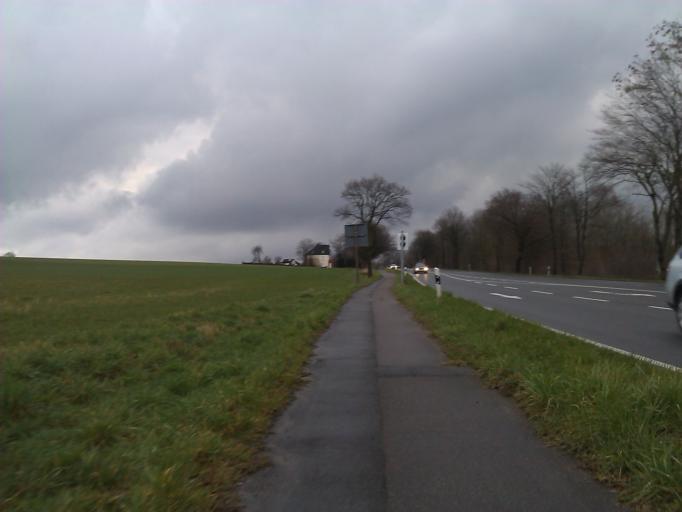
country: DE
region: North Rhine-Westphalia
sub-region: Regierungsbezirk Dusseldorf
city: Heiligenhaus
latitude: 51.3818
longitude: 6.9366
